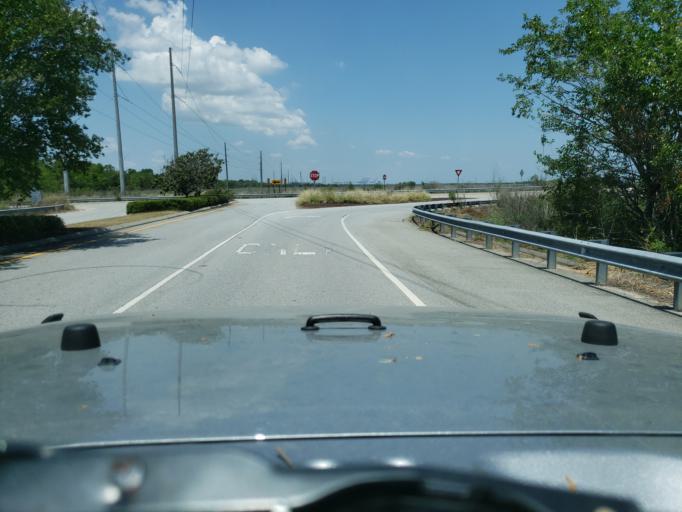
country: US
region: Georgia
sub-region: Chatham County
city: Savannah
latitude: 32.0969
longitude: -81.0951
